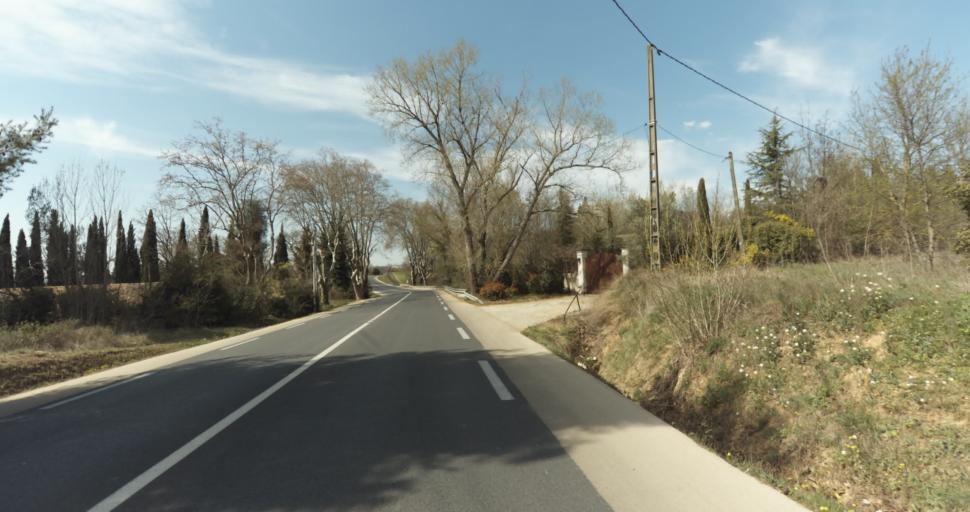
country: FR
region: Provence-Alpes-Cote d'Azur
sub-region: Departement des Bouches-du-Rhone
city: Eguilles
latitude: 43.5370
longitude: 5.3858
